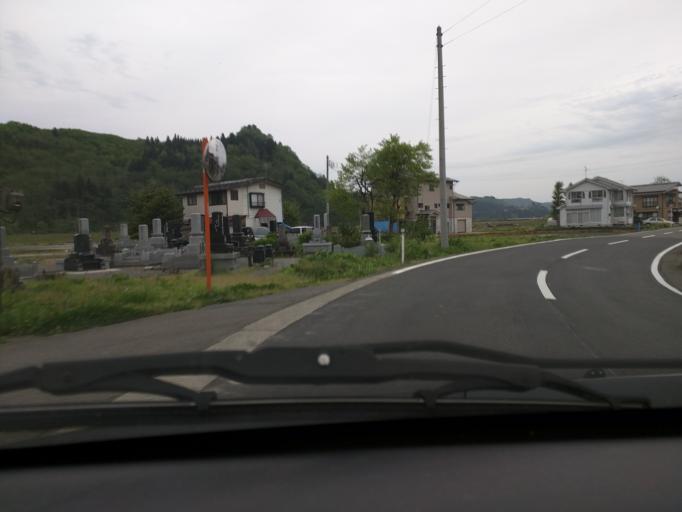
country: JP
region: Niigata
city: Muikamachi
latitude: 37.2017
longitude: 138.9536
